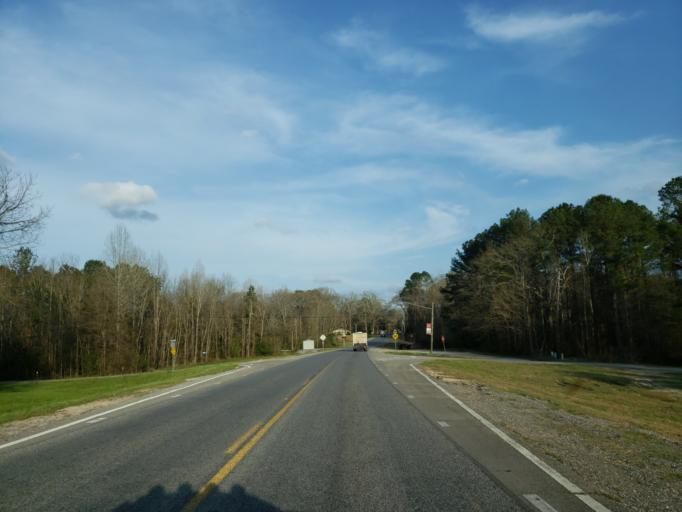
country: US
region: Mississippi
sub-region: Clarke County
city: Stonewall
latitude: 32.1762
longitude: -88.8155
